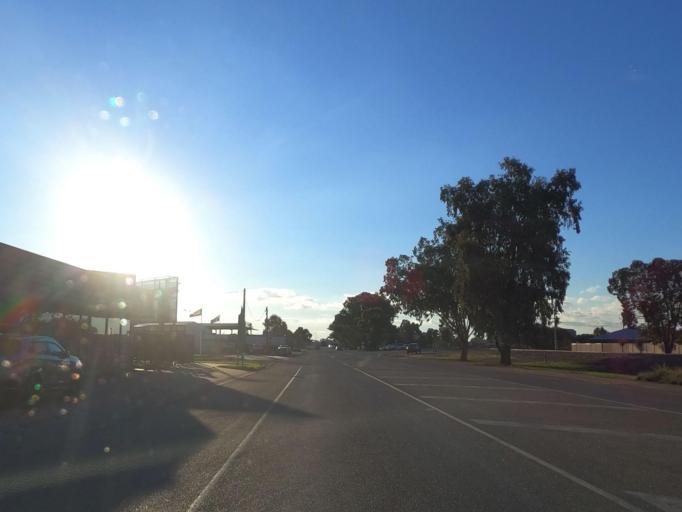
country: AU
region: Victoria
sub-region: Swan Hill
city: Swan Hill
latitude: -35.3311
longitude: 143.5570
